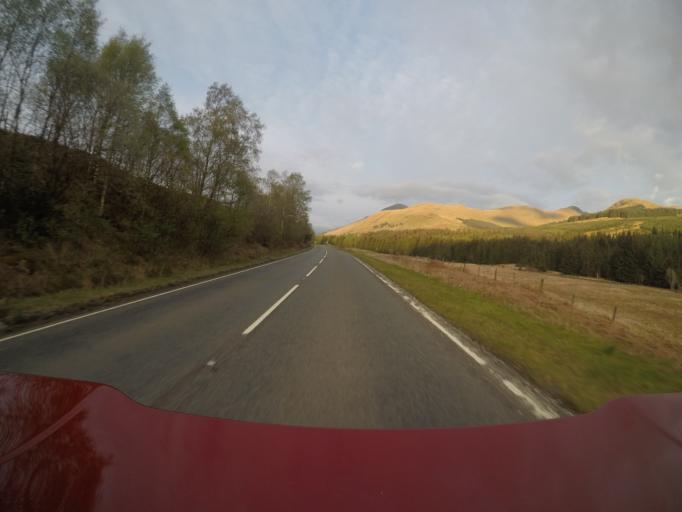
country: GB
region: Scotland
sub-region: Argyll and Bute
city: Garelochhead
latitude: 56.3822
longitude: -4.6330
